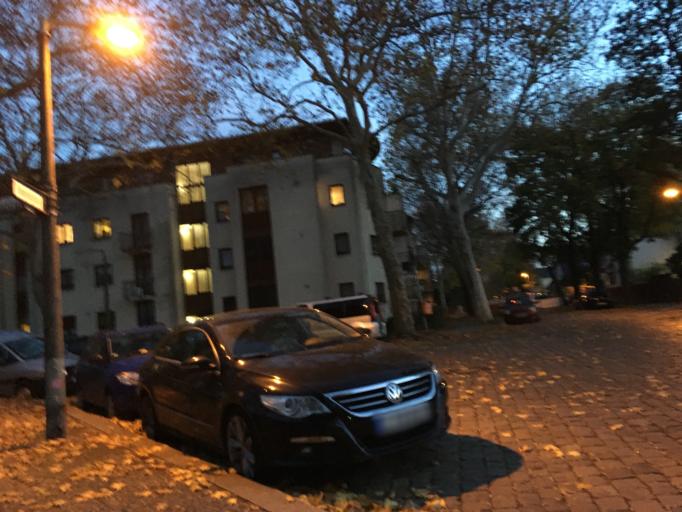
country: DE
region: Berlin
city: Niederschonhausen
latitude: 52.5841
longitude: 13.3883
